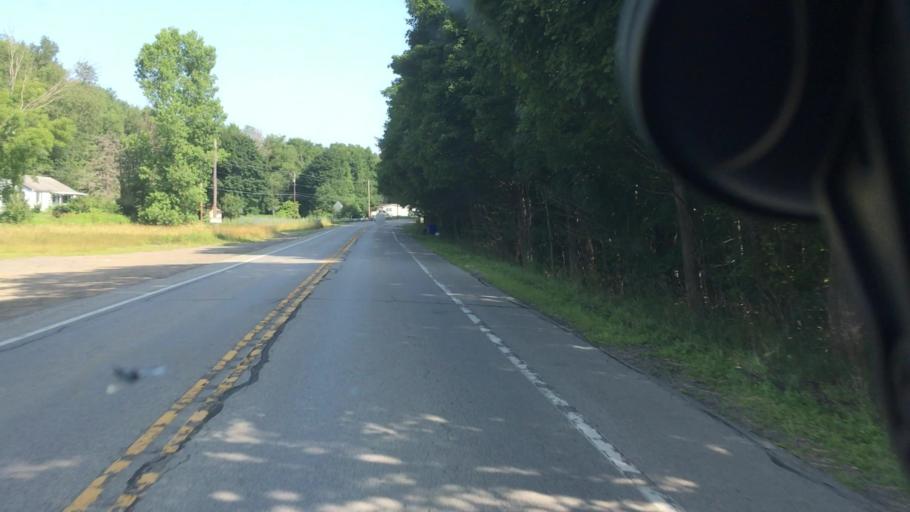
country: US
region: Pennsylvania
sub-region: Butler County
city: Slippery Rock
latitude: 41.0262
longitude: -80.1892
